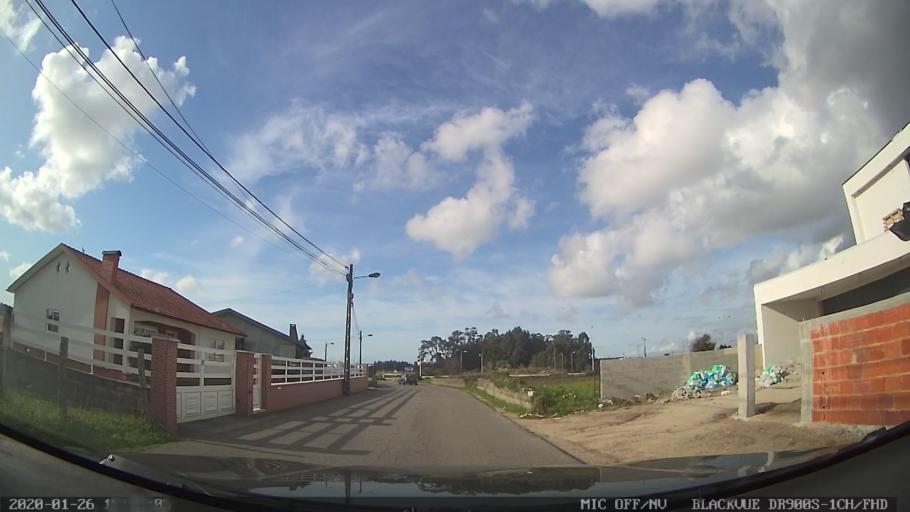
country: PT
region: Aveiro
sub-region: Aveiro
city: Aradas
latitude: 40.6305
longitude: -8.6296
